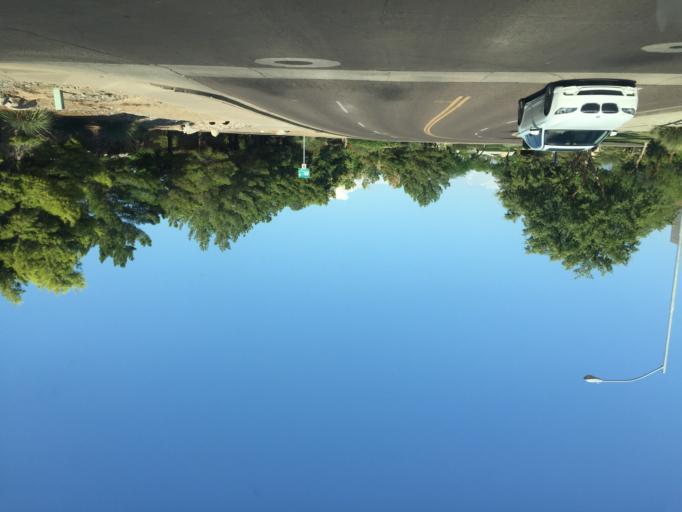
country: US
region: Arizona
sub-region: Maricopa County
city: Paradise Valley
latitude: 33.5955
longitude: -111.9779
